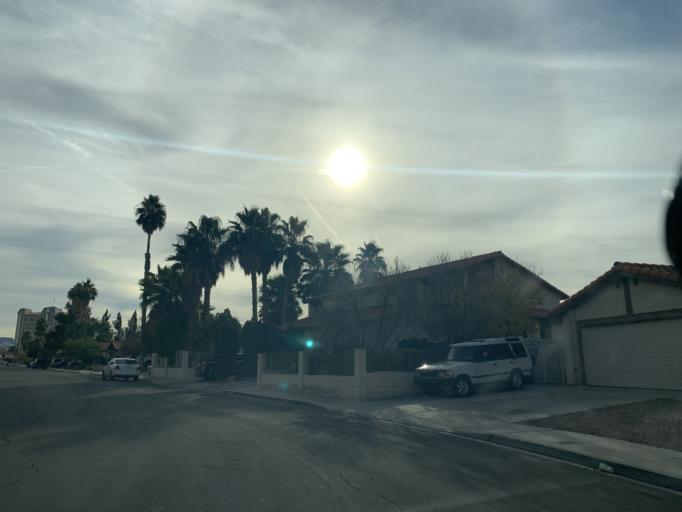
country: US
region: Nevada
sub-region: Clark County
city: Las Vegas
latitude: 36.1494
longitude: -115.1747
